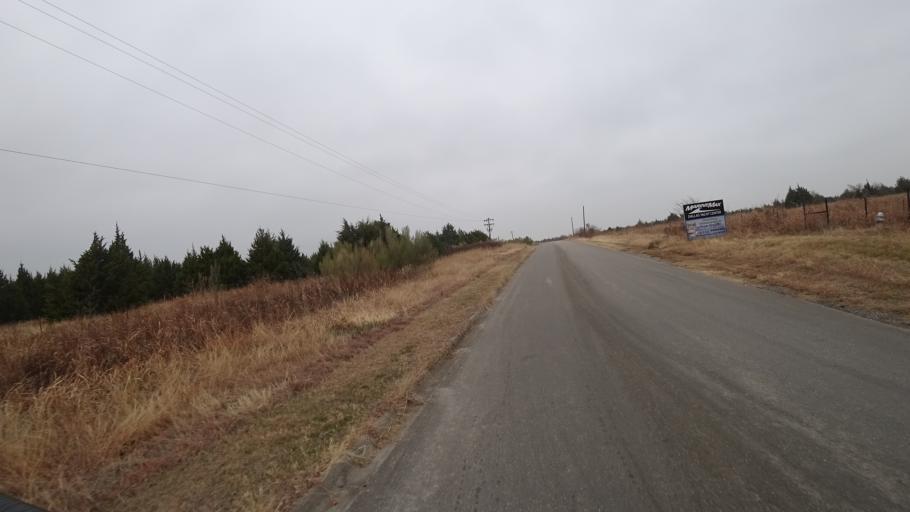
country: US
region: Texas
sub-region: Denton County
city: The Colony
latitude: 33.0651
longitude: -96.9173
